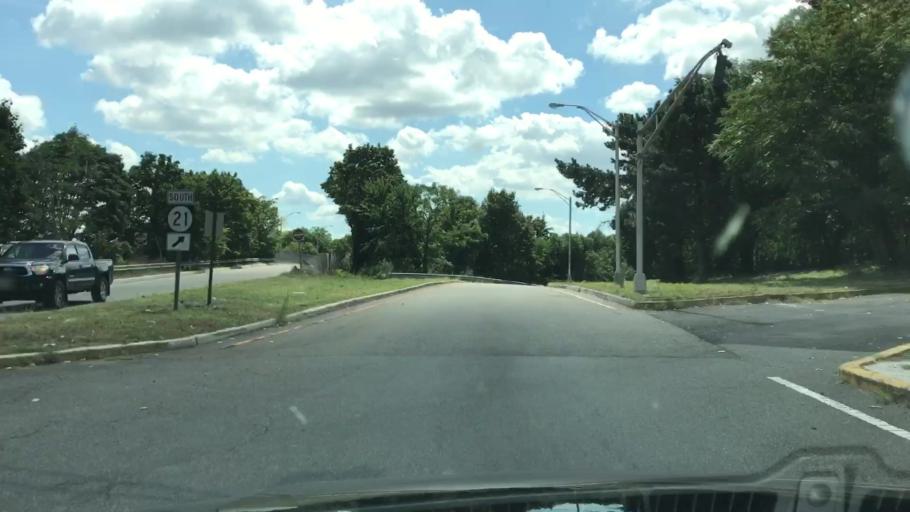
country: US
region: New Jersey
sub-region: Passaic County
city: Passaic
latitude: 40.8588
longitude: -74.1220
